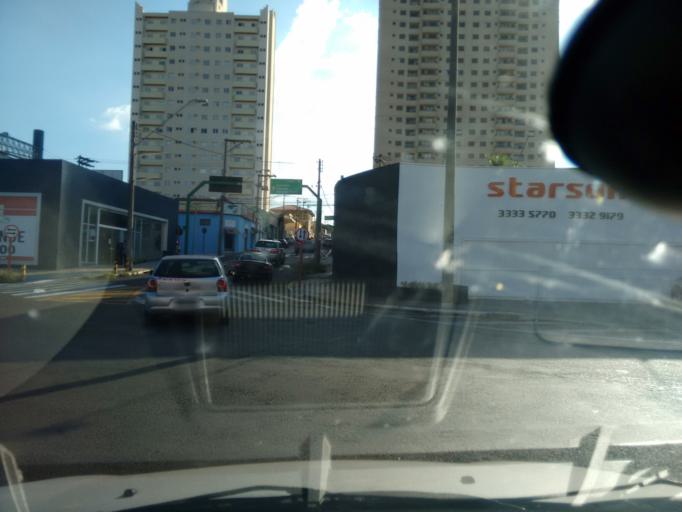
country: BR
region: Sao Paulo
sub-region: Araraquara
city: Araraquara
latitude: -21.7971
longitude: -48.1730
